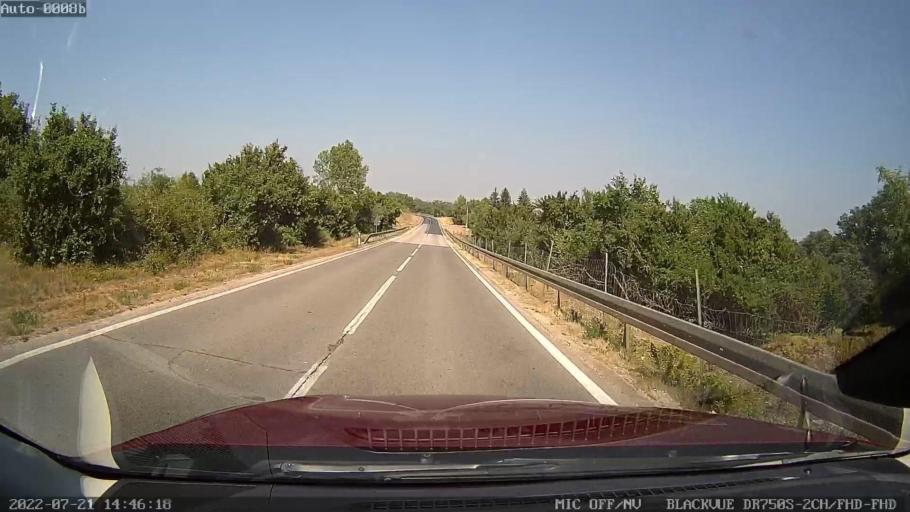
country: HR
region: Istarska
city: Pazin
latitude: 45.1356
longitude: 13.8987
